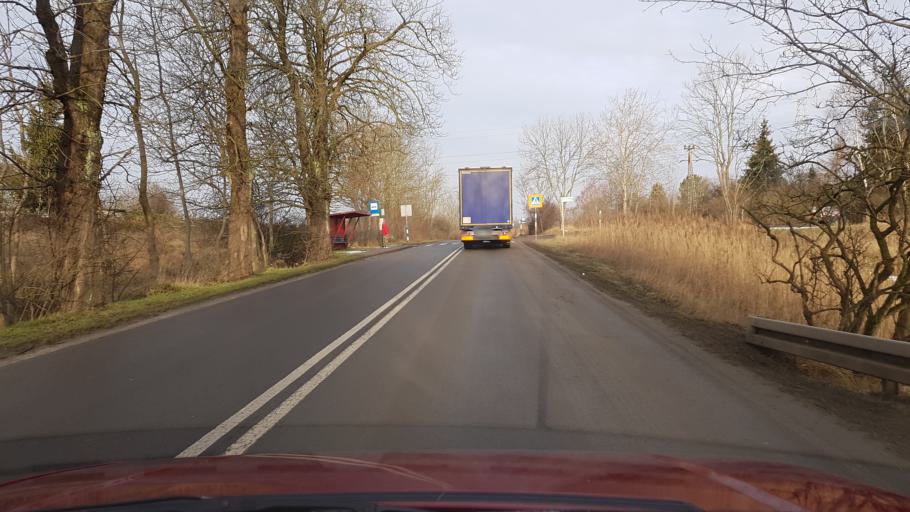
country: PL
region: West Pomeranian Voivodeship
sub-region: Powiat policki
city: Police
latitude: 53.4976
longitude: 14.5816
